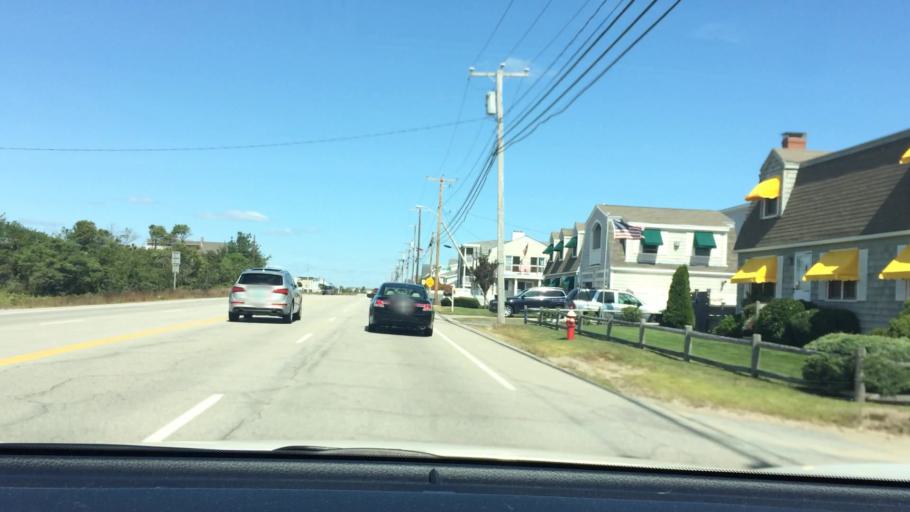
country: US
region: New Hampshire
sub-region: Rockingham County
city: Hampton Beach
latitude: 42.8744
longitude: -70.8184
